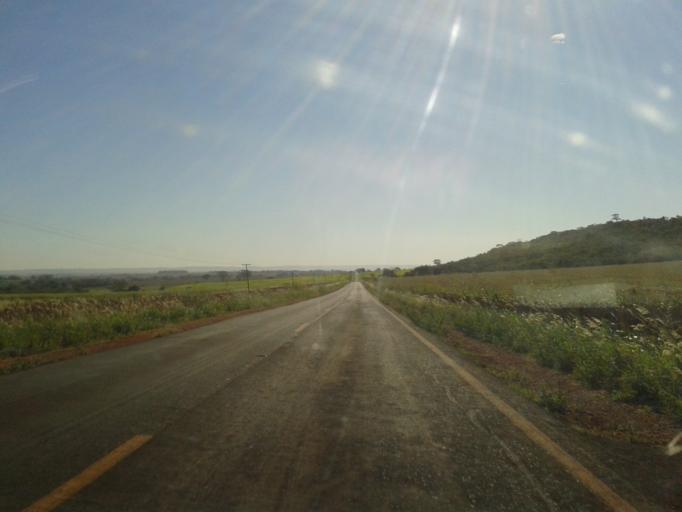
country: BR
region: Minas Gerais
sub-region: Capinopolis
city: Capinopolis
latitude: -18.6314
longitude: -49.5398
